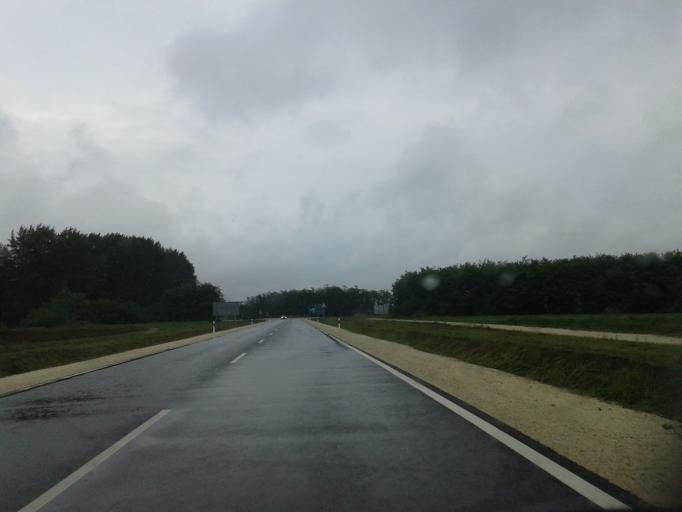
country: HU
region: Csongrad
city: Morahalom
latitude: 46.2250
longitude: 19.9059
